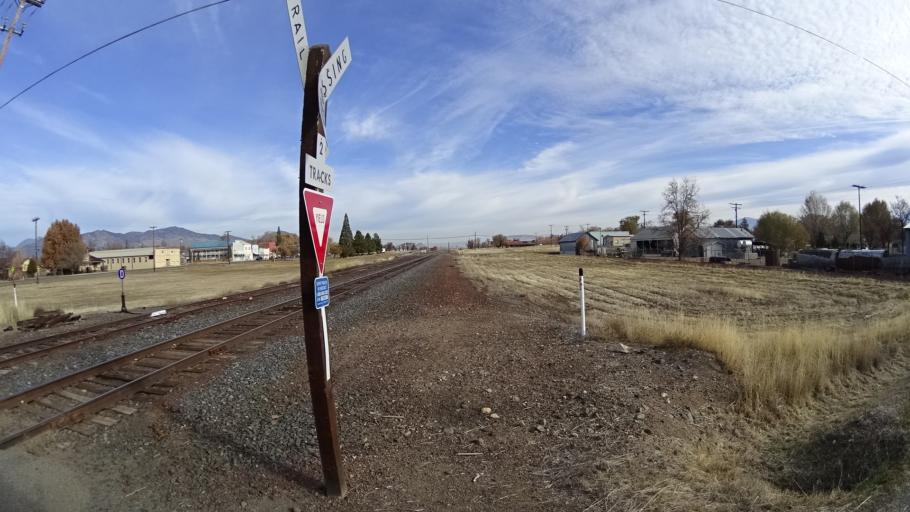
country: US
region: California
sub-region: Siskiyou County
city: Montague
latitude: 41.7255
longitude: -122.5283
